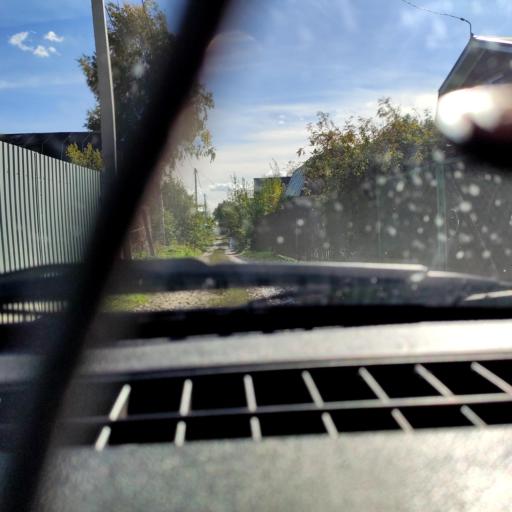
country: RU
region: Bashkortostan
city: Iglino
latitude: 54.7769
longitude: 56.2086
